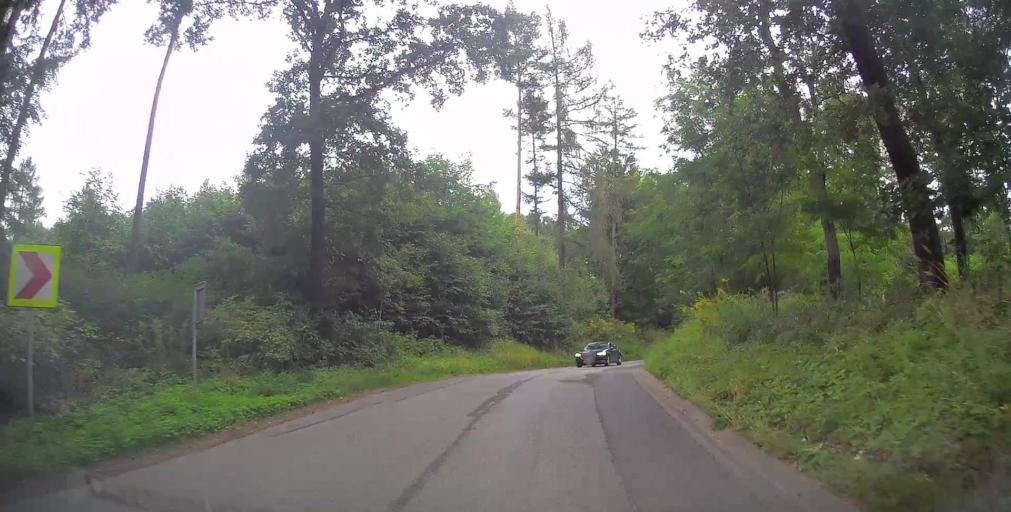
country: PL
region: Lesser Poland Voivodeship
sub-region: Powiat chrzanowski
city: Grojec
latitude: 50.0739
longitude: 19.5507
